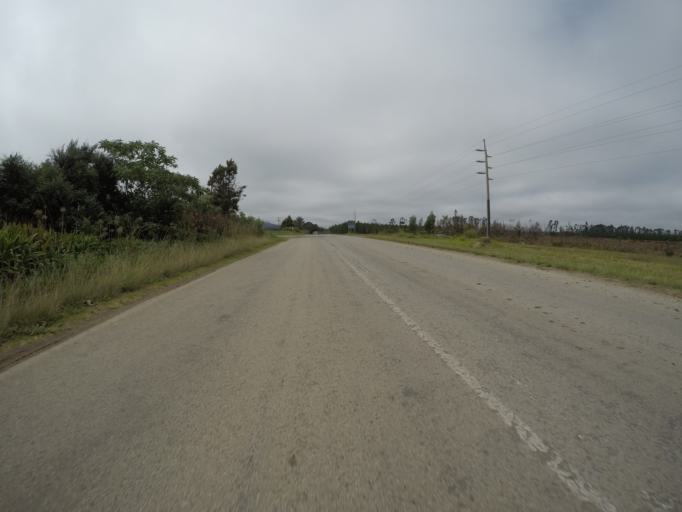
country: ZA
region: Eastern Cape
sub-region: Cacadu District Municipality
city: Kareedouw
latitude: -33.9965
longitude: 24.1403
